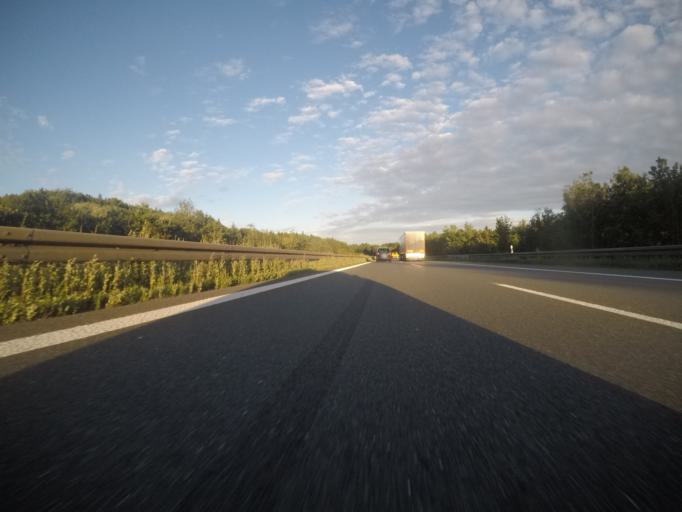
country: DE
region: Bavaria
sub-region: Regierungsbezirk Mittelfranken
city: Altdorf
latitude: 49.4027
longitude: 11.3704
